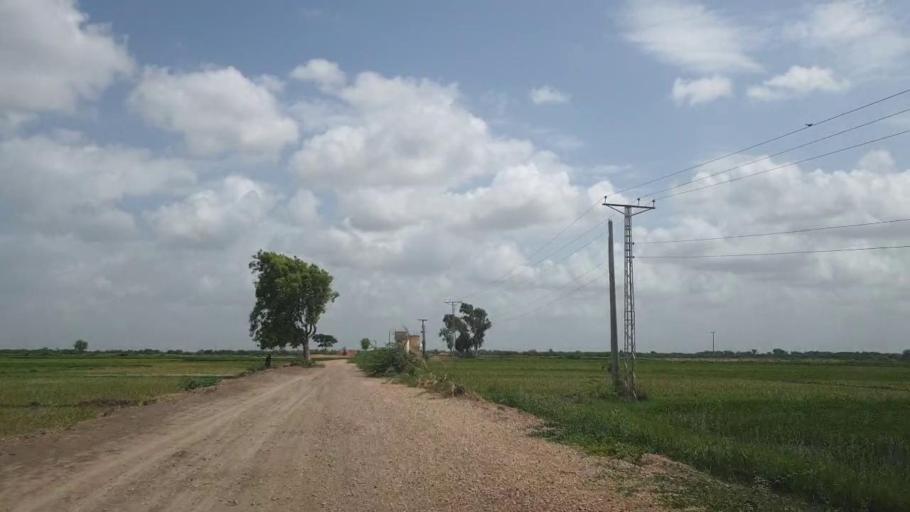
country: PK
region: Sindh
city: Tando Bago
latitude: 24.6483
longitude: 68.9936
